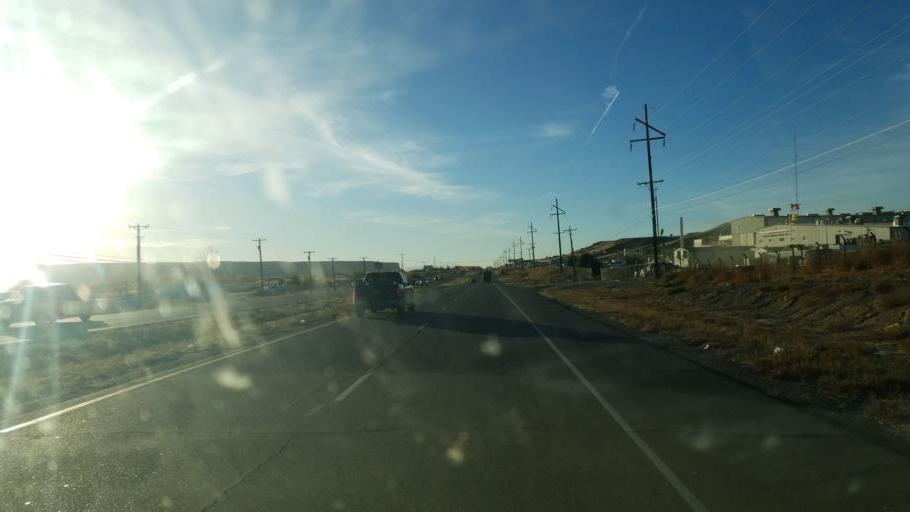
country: US
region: New Mexico
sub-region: San Juan County
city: Lee Acres
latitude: 36.7042
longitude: -108.1059
